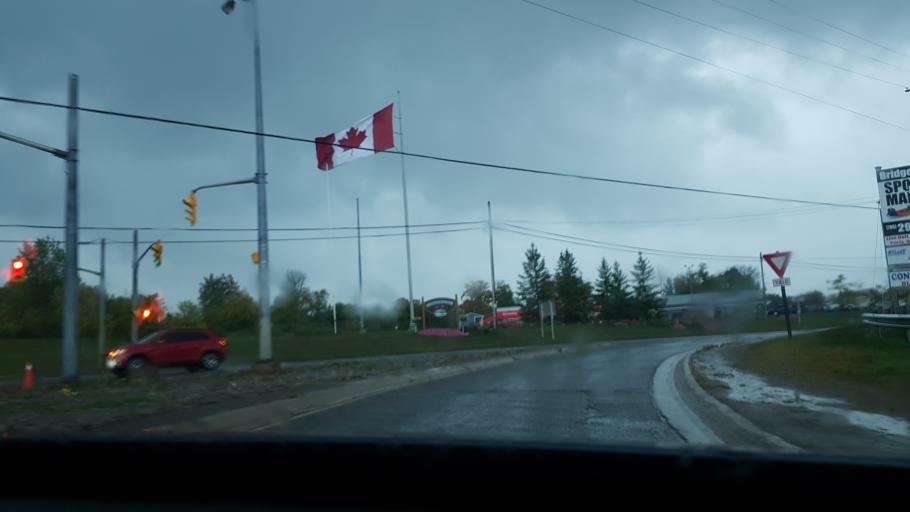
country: CA
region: Ontario
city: Peterborough
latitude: 44.3848
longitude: -78.3838
